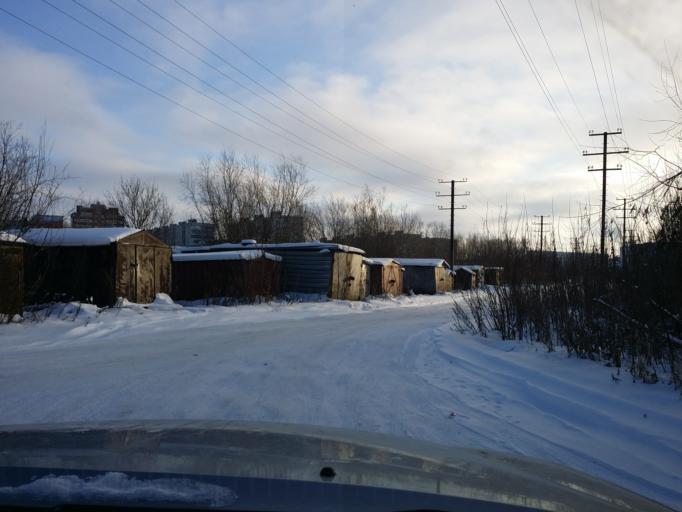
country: RU
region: Khanty-Mansiyskiy Avtonomnyy Okrug
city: Megion
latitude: 61.0433
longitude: 76.1029
